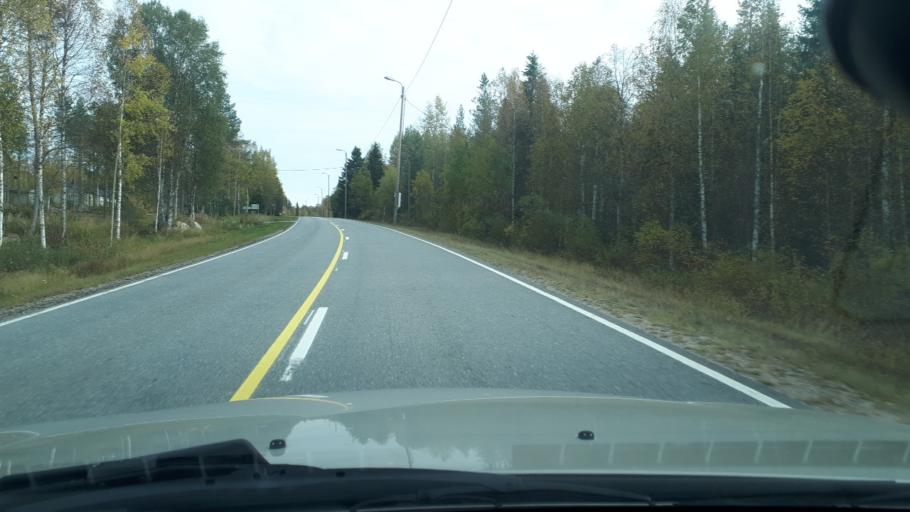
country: FI
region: Lapland
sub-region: Rovaniemi
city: Ranua
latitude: 65.9991
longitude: 26.2150
